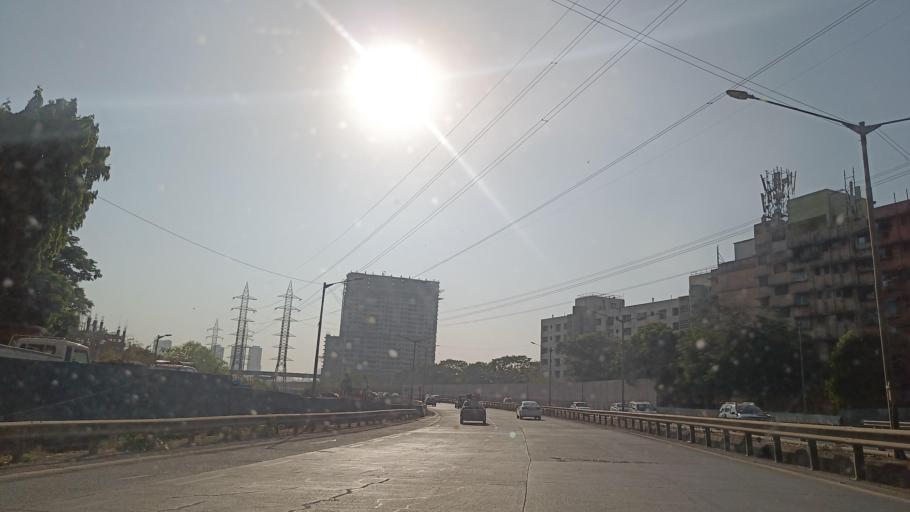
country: IN
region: Maharashtra
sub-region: Mumbai Suburban
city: Mumbai
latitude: 19.0335
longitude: 72.8998
